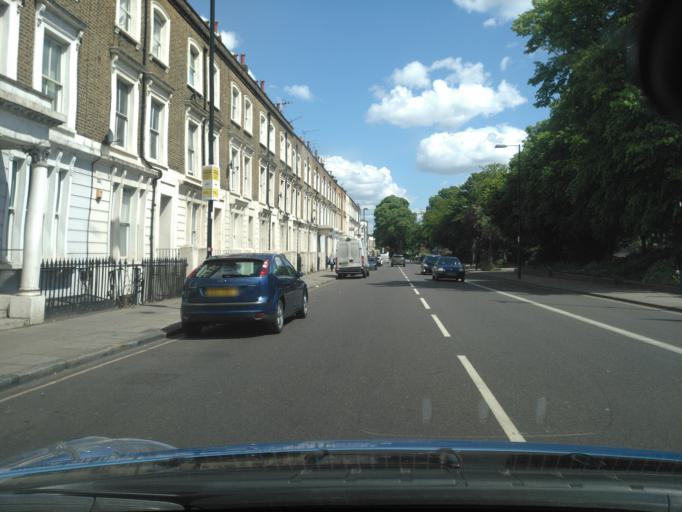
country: GB
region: England
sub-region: Greater London
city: Islington
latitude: 51.5463
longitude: -0.1005
